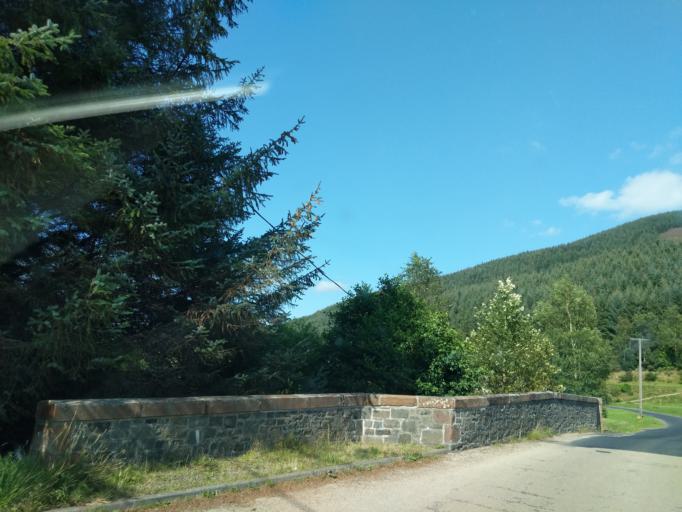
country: GB
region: Scotland
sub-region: The Scottish Borders
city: Innerleithen
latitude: 55.6373
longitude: -3.0571
